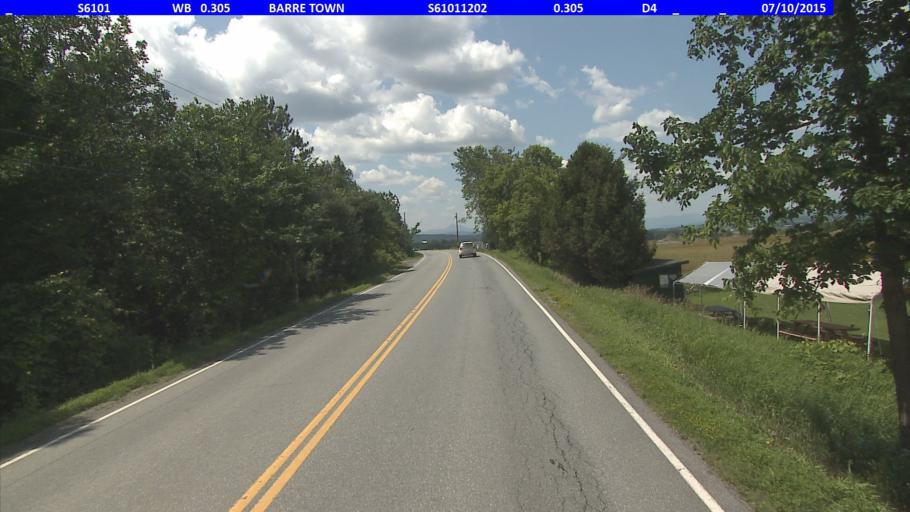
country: US
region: Vermont
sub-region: Washington County
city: South Barre
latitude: 44.1888
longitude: -72.5401
